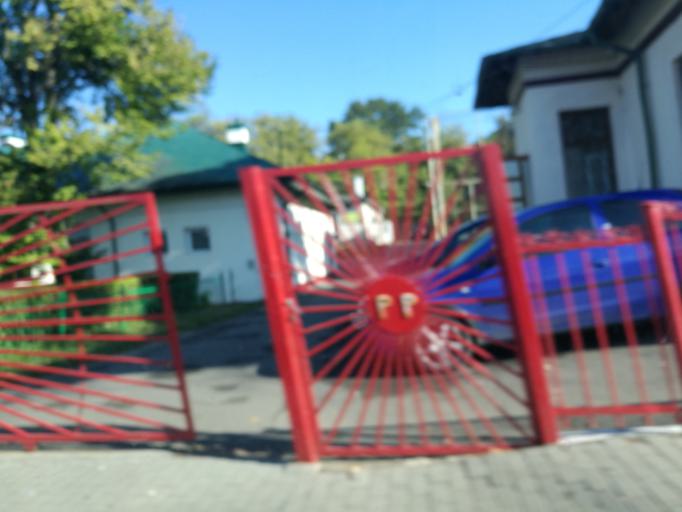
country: RO
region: Iasi
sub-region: Municipiul Iasi
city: Iasi
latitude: 47.1731
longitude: 27.5615
